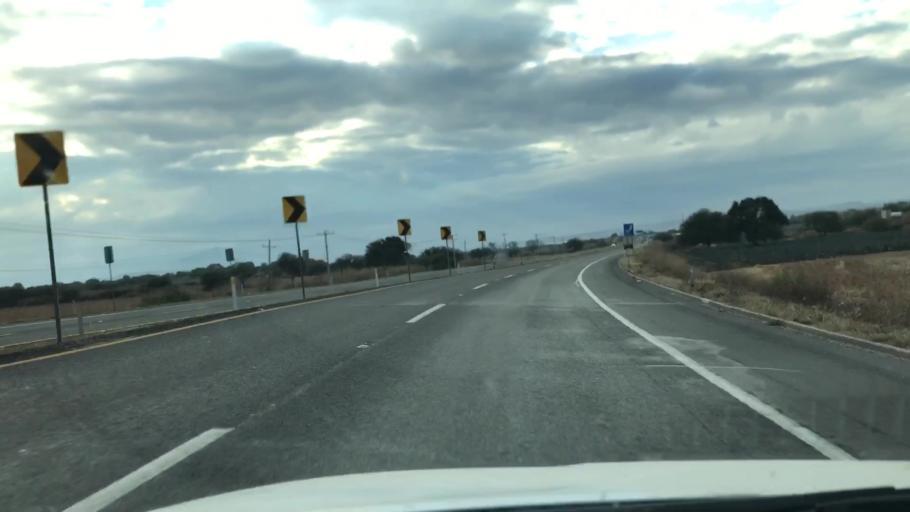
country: MX
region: Guanajuato
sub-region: Penjamo
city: Mezquite de Luna
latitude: 20.3778
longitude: -101.8505
